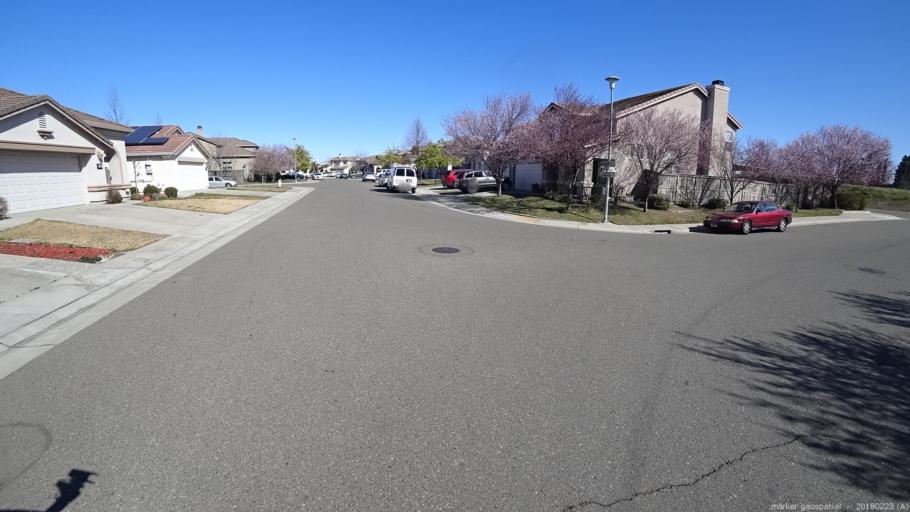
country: US
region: California
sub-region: Sacramento County
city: Antelope
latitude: 38.7049
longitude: -121.3536
